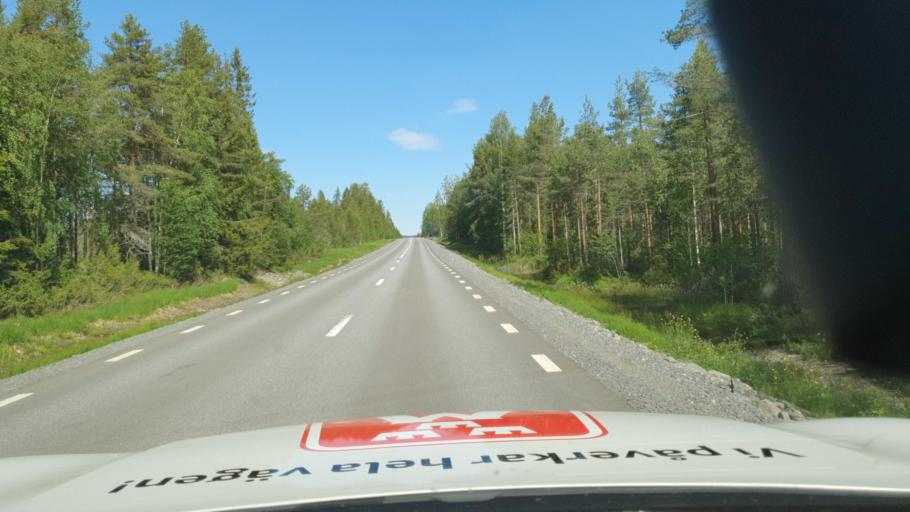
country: SE
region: Vaesterbotten
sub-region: Skelleftea Kommun
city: Langsele
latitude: 64.7613
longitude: 20.3397
